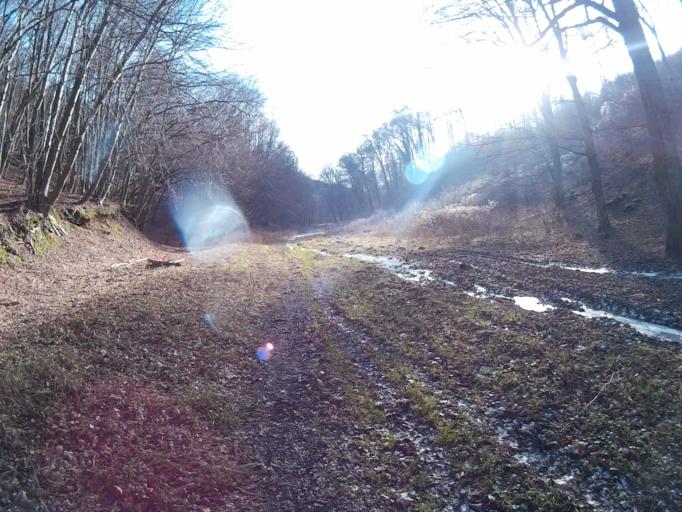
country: HU
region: Komarom-Esztergom
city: Tatabanya
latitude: 47.5035
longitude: 18.4114
